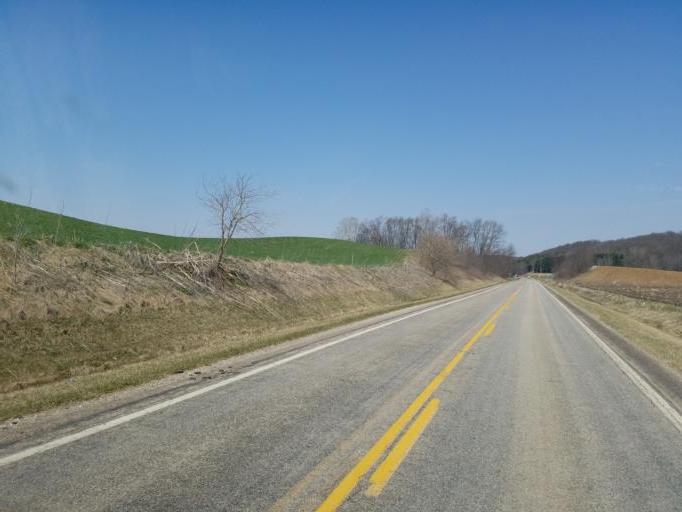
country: US
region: Ohio
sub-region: Ashland County
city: Loudonville
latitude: 40.6946
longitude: -82.1496
